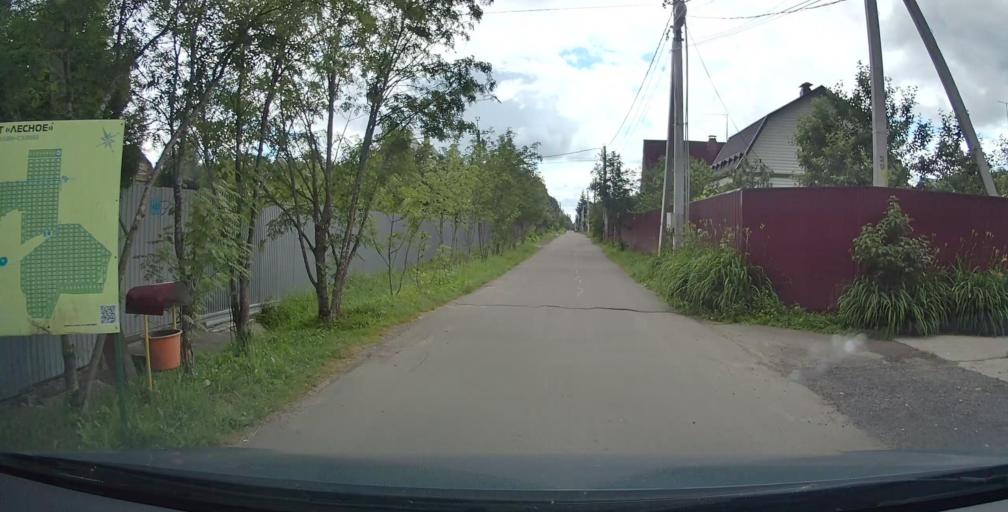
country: RU
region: Moskovskaya
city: Selyatino
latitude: 55.3957
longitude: 37.0096
